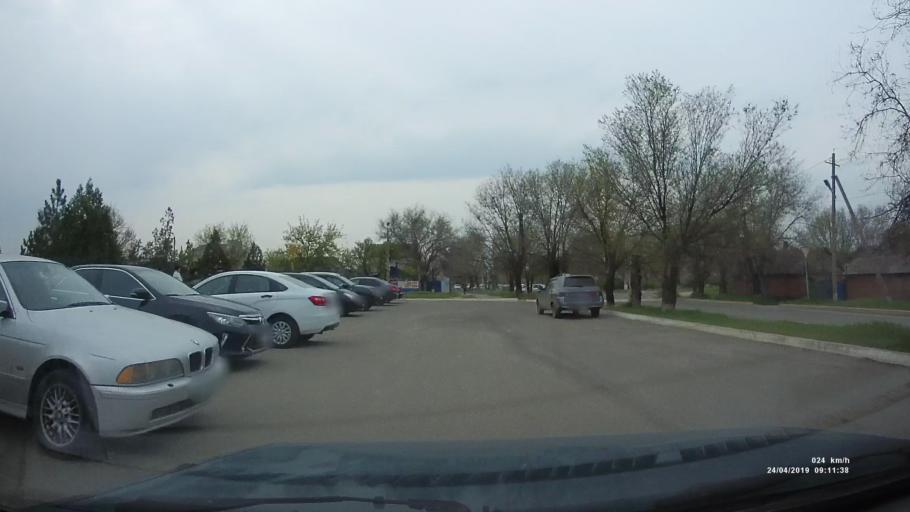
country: RU
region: Kalmykiya
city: Elista
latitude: 46.3088
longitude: 44.2827
